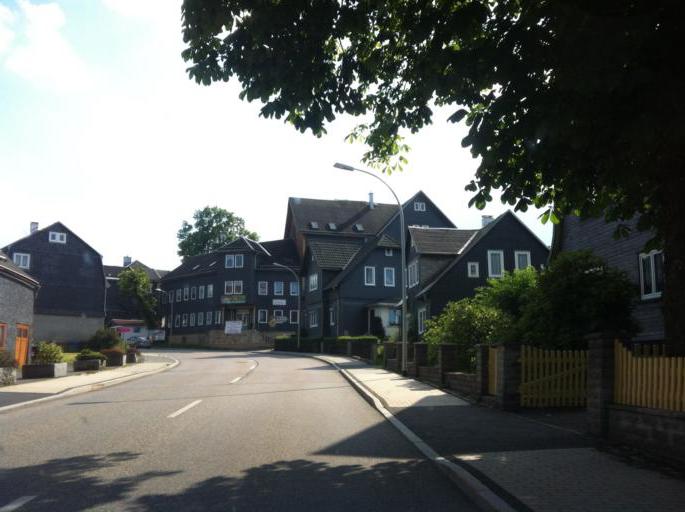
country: DE
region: Thuringia
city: Neuhaus am Rennweg
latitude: 50.5127
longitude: 11.1400
